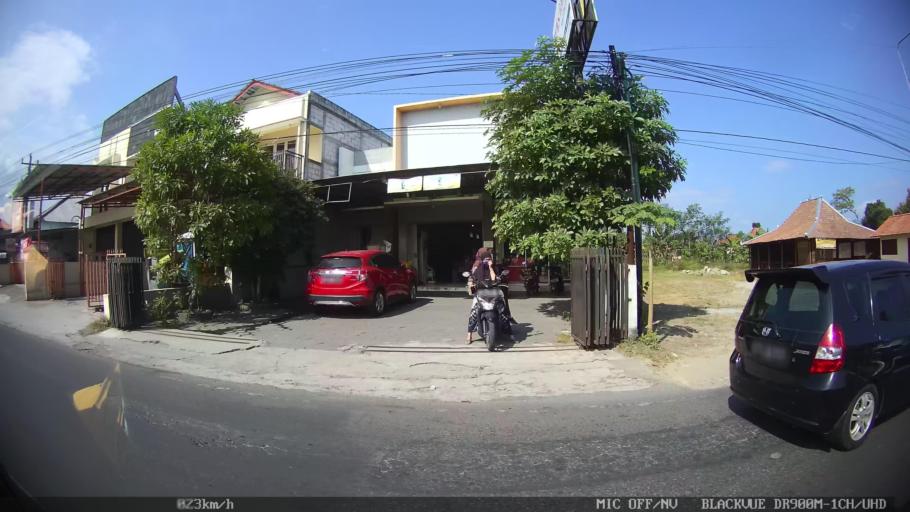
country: ID
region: Daerah Istimewa Yogyakarta
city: Sewon
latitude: -7.8719
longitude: 110.3915
